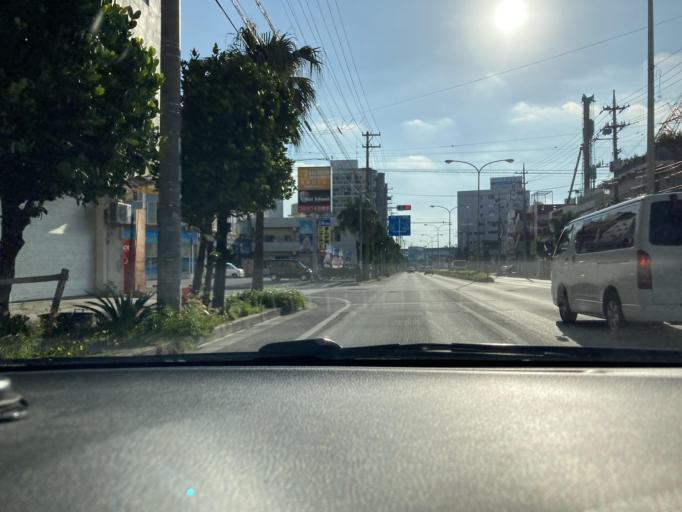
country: JP
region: Okinawa
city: Naha-shi
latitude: 26.2413
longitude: 127.6866
